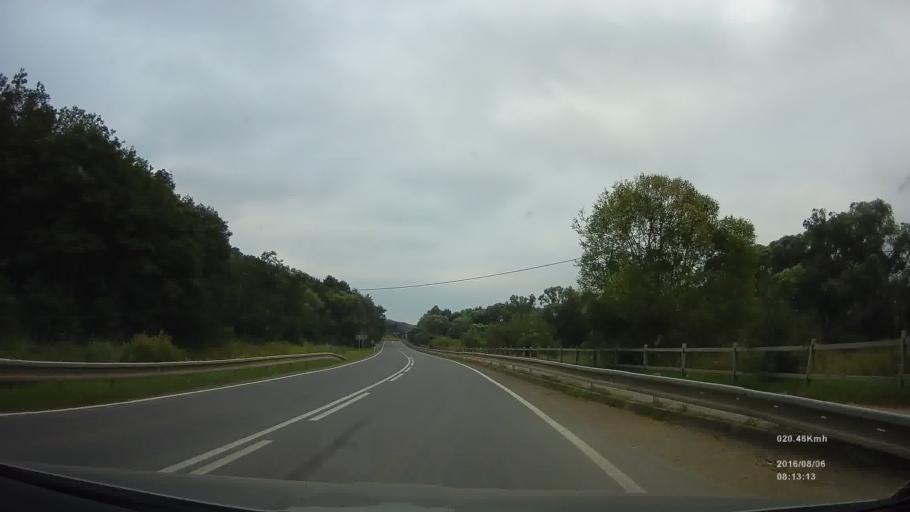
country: SK
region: Presovsky
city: Stropkov
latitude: 49.2254
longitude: 21.6640
